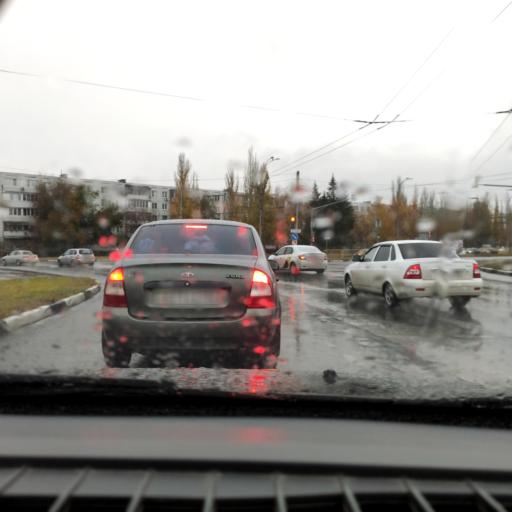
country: RU
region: Samara
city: Tol'yatti
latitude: 53.5278
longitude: 49.2977
